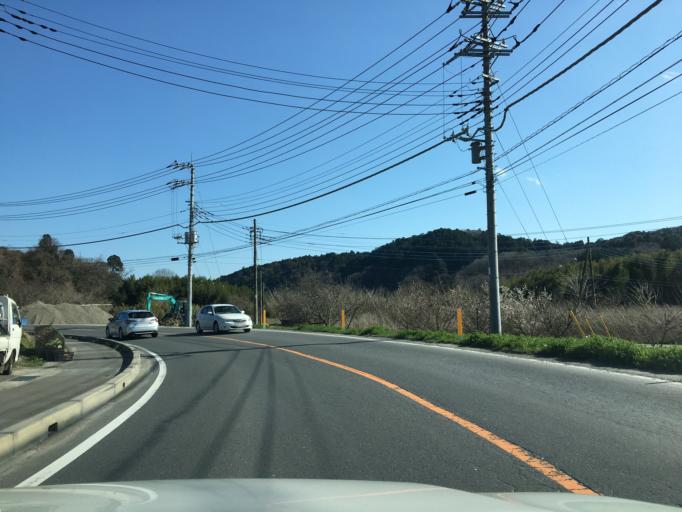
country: JP
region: Ibaraki
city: Omiya
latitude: 36.5551
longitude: 140.3196
